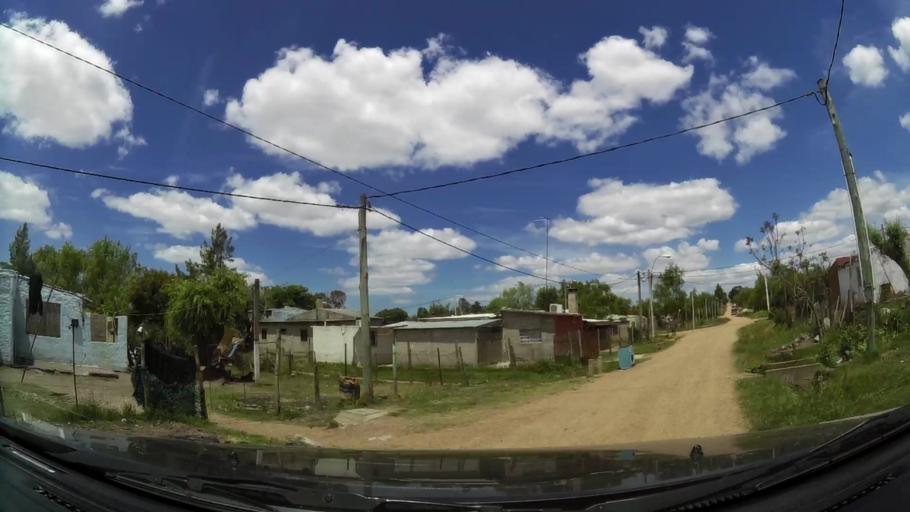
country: UY
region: Canelones
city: Colonia Nicolich
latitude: -34.8207
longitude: -56.0000
